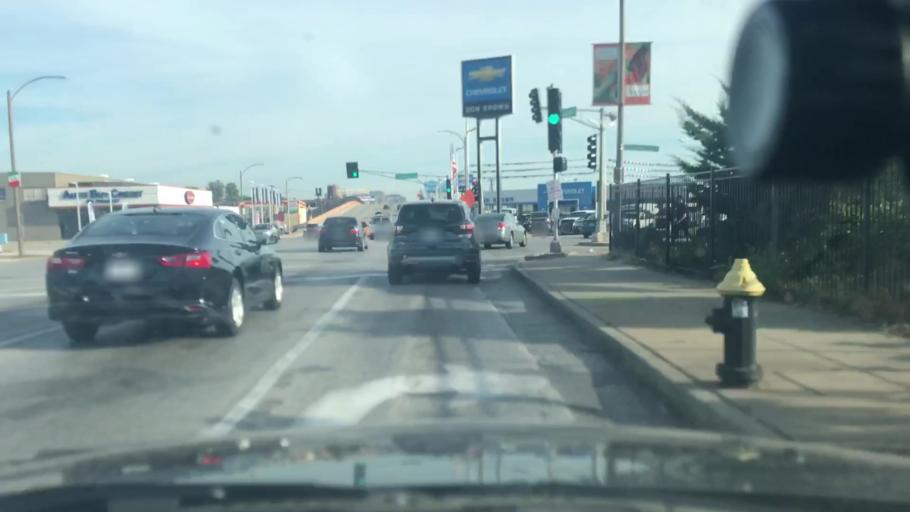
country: US
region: Missouri
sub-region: Saint Louis County
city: Richmond Heights
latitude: 38.6124
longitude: -90.2676
